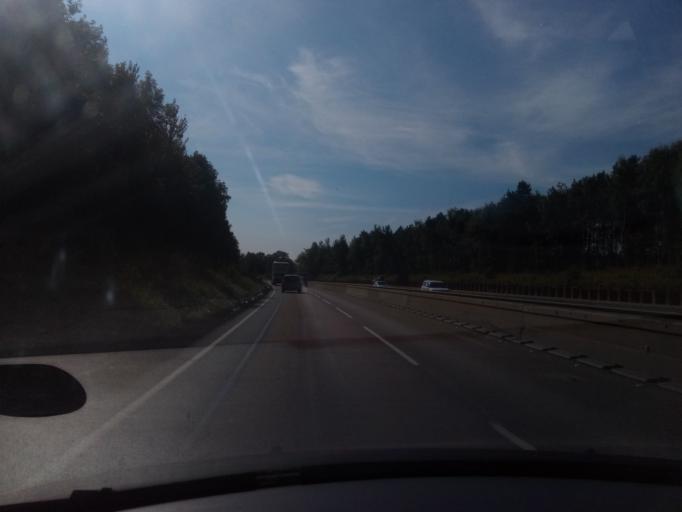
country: GB
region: England
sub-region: Stockton-on-Tees
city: Billingham
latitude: 54.6092
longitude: -1.3191
